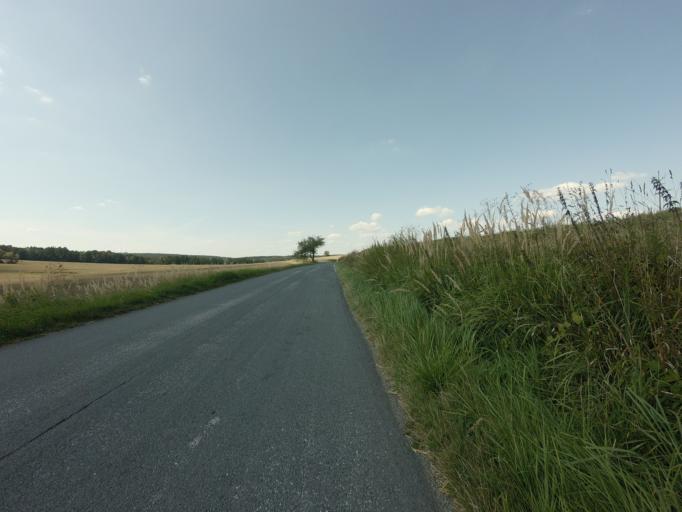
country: CZ
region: Jihocesky
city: Tyn nad Vltavou
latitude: 49.1424
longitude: 14.4474
